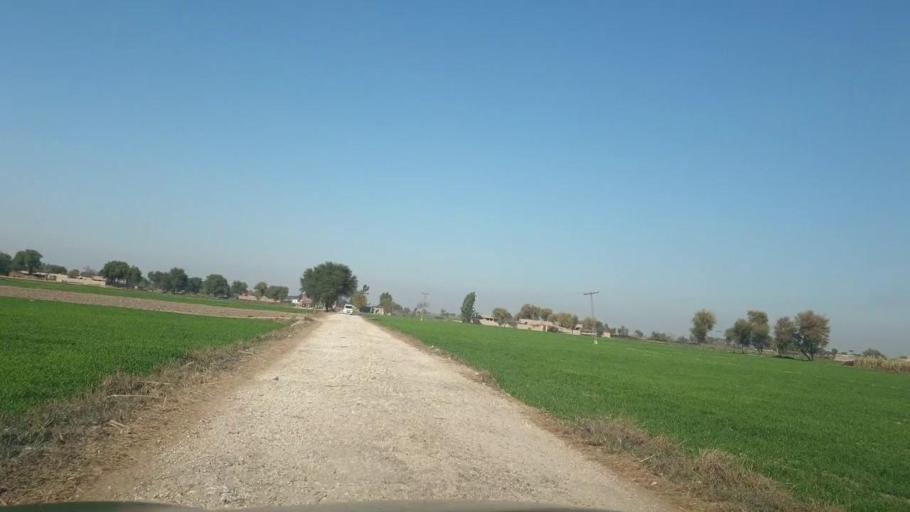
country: PK
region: Sindh
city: Mirpur Mathelo
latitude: 28.0013
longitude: 69.4795
